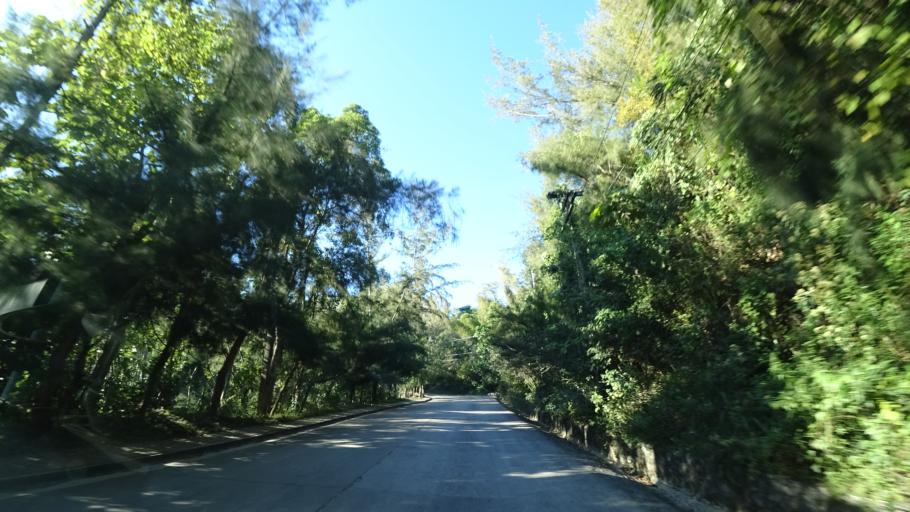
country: HT
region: Ouest
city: Port-au-Prince
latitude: 18.4980
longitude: -72.3493
